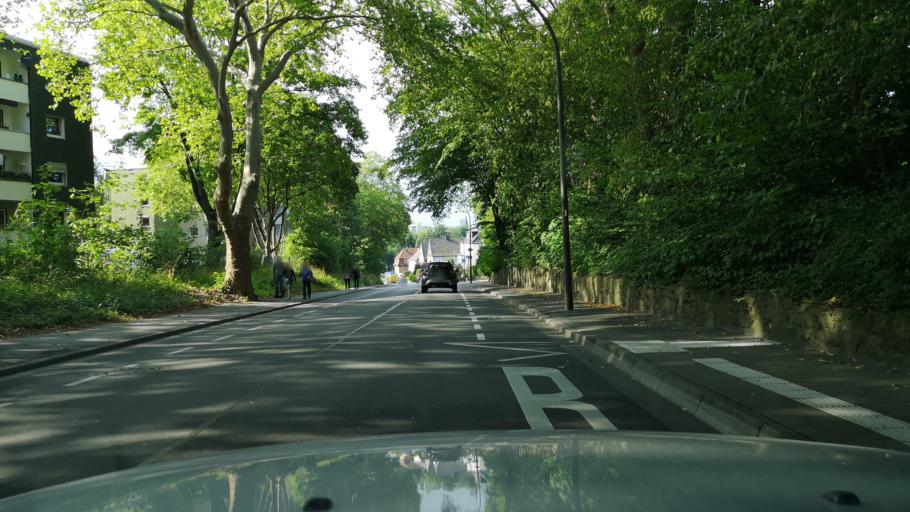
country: DE
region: North Rhine-Westphalia
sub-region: Regierungsbezirk Arnsberg
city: Dortmund
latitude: 51.4777
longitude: 7.5080
